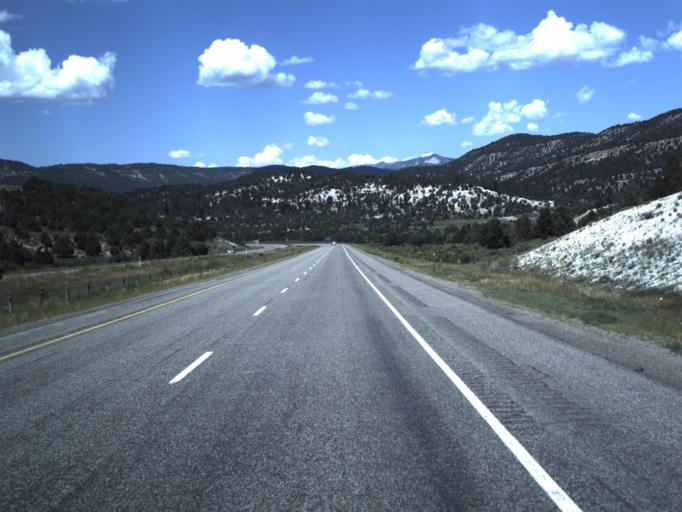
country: US
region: Utah
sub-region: Sevier County
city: Salina
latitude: 38.8691
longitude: -111.5523
